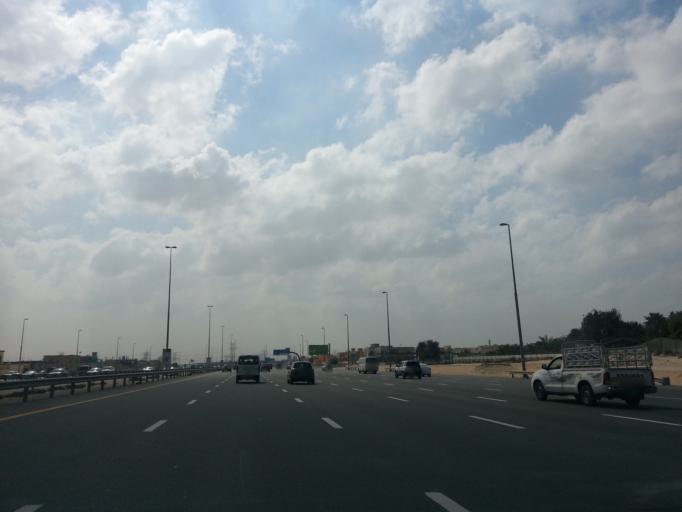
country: AE
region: Dubai
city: Dubai
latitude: 25.1557
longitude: 55.2613
